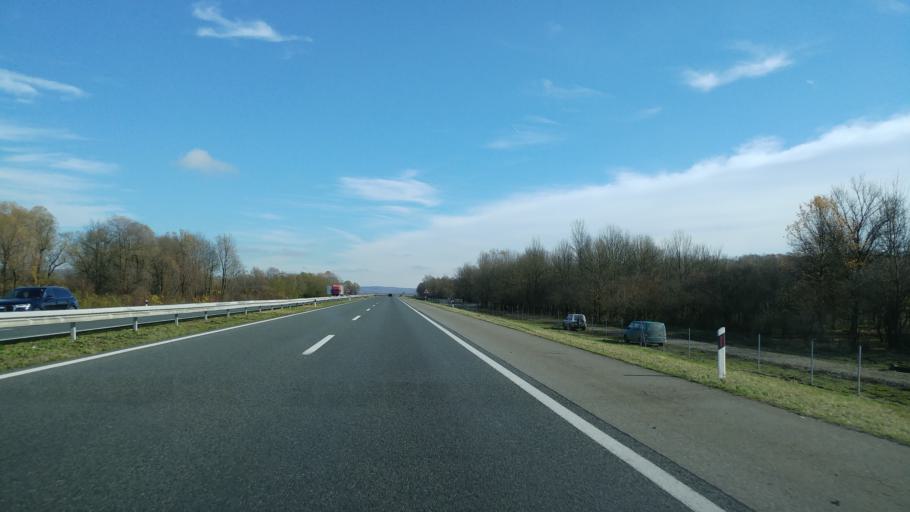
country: HR
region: Sisacko-Moslavacka
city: Novska
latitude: 45.3054
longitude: 17.0296
